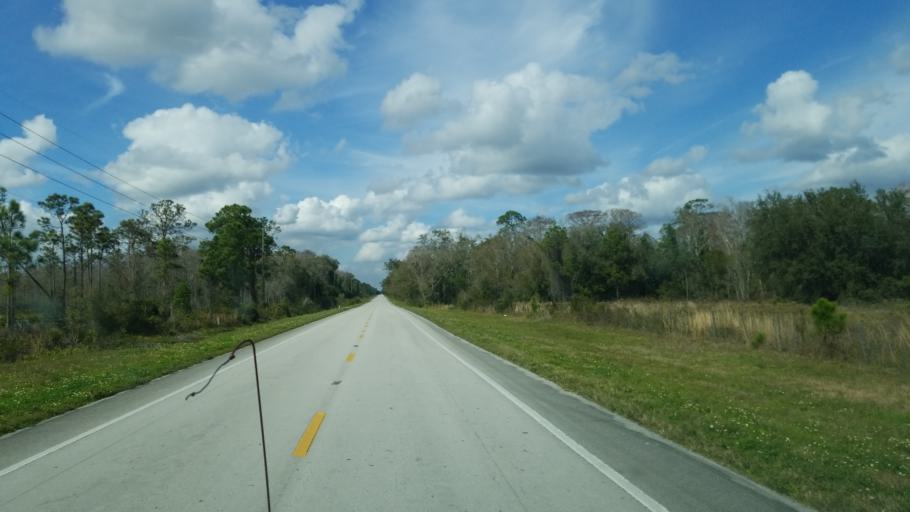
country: US
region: Florida
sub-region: Brevard County
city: June Park
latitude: 27.9631
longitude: -81.0047
